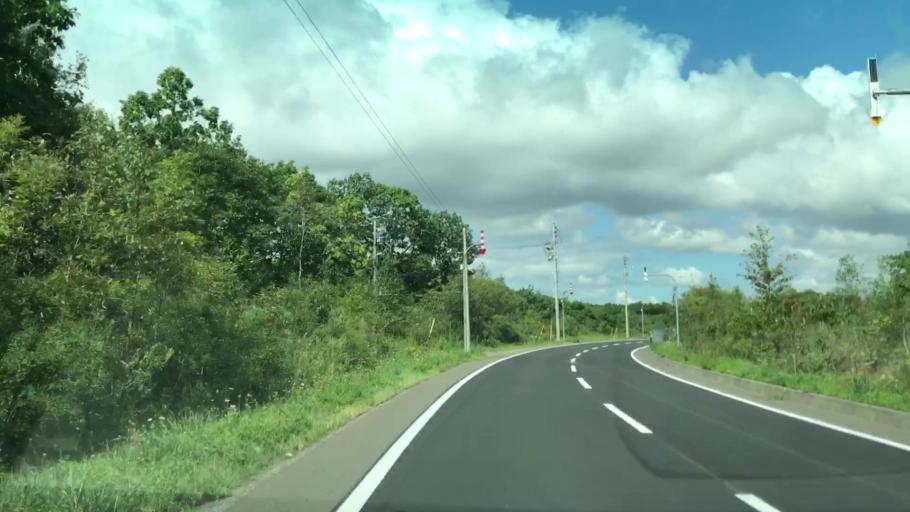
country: JP
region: Hokkaido
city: Chitose
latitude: 42.7634
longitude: 141.6656
